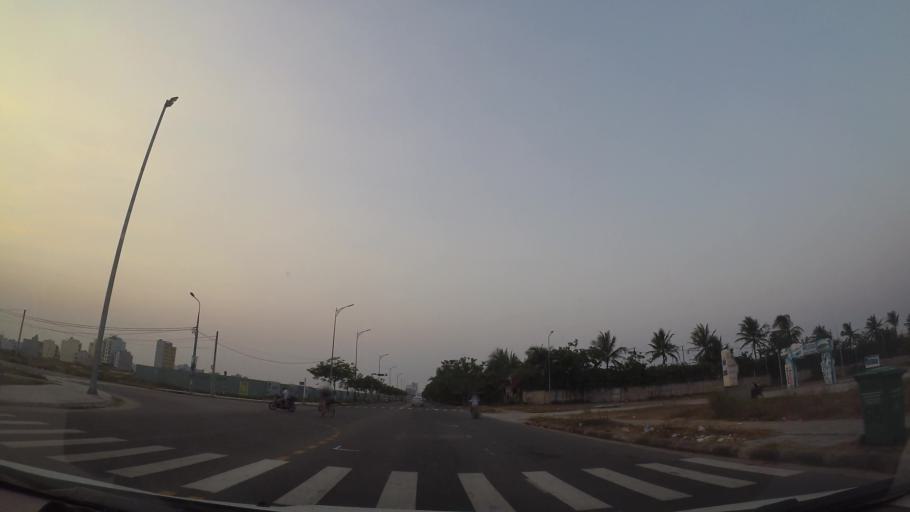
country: VN
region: Da Nang
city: Ngu Hanh Son
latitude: 16.0154
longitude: 108.2610
